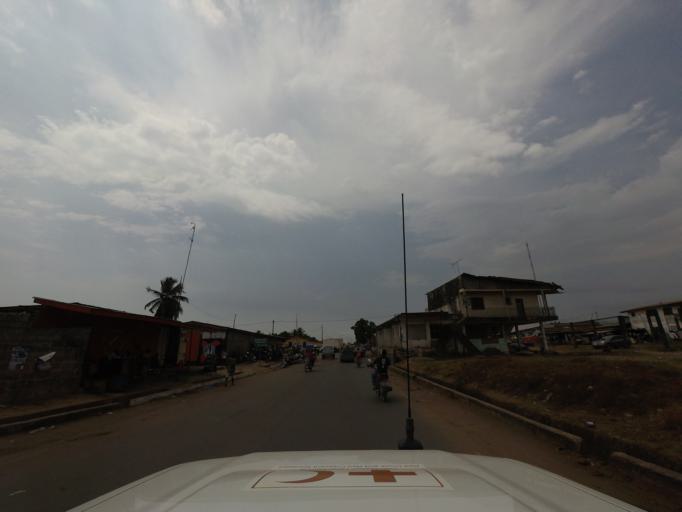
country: LR
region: Montserrado
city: Monrovia
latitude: 6.2961
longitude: -10.6831
